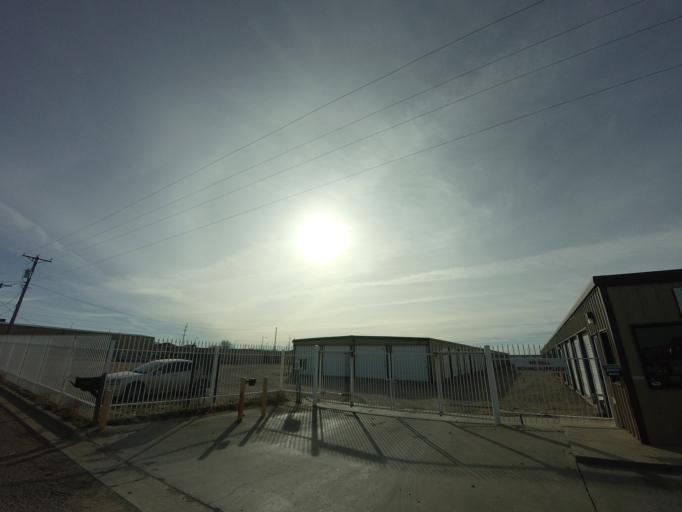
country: US
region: New Mexico
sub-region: Curry County
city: Clovis
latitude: 34.4171
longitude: -103.2332
